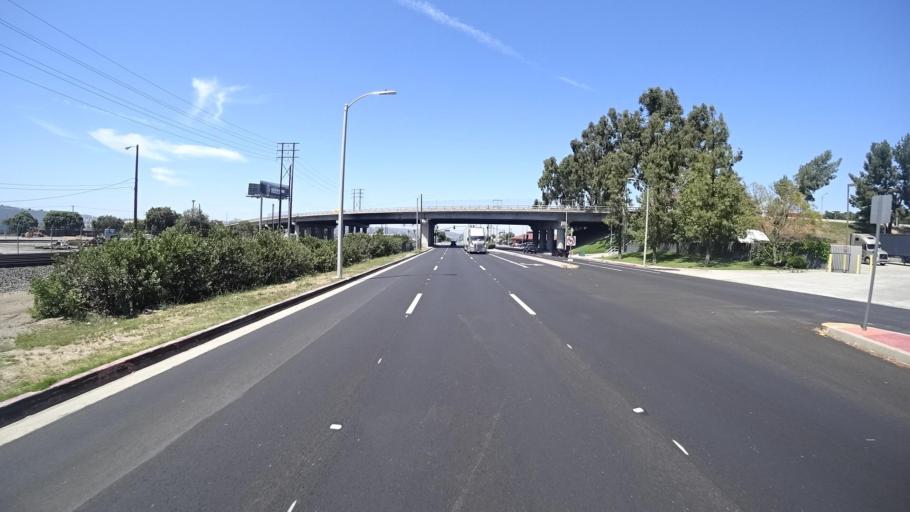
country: US
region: California
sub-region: Los Angeles County
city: South San Jose Hills
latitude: 34.0089
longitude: -117.9244
